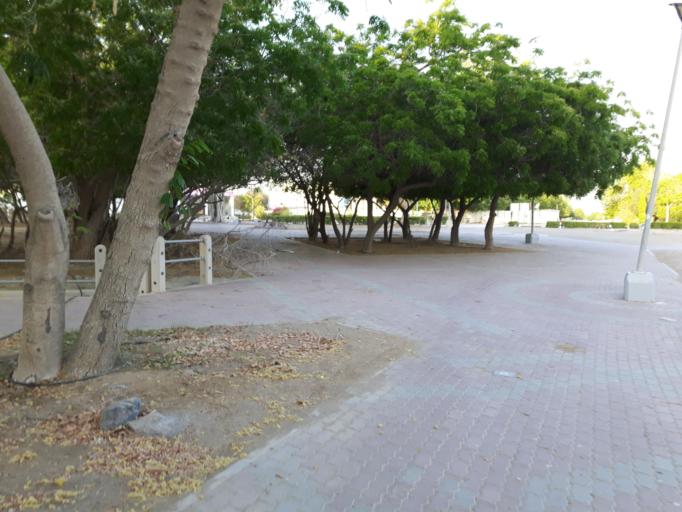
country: OM
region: Muhafazat Masqat
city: Bawshar
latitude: 23.6133
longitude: 58.4621
